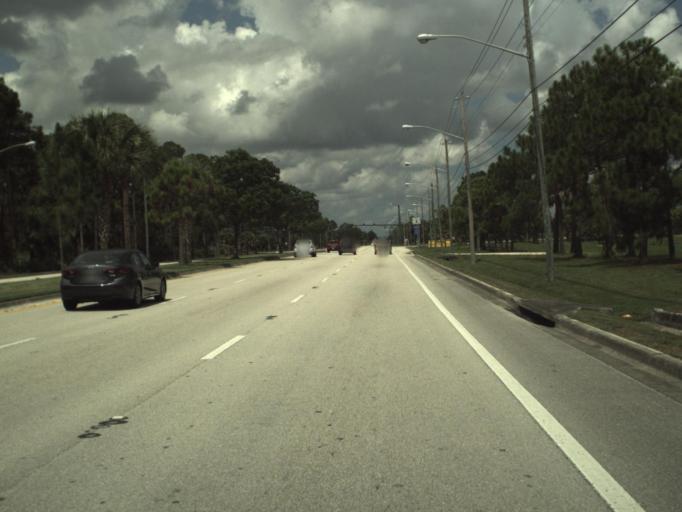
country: US
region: Florida
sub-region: Palm Beach County
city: Greenacres City
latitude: 26.6512
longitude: -80.1619
